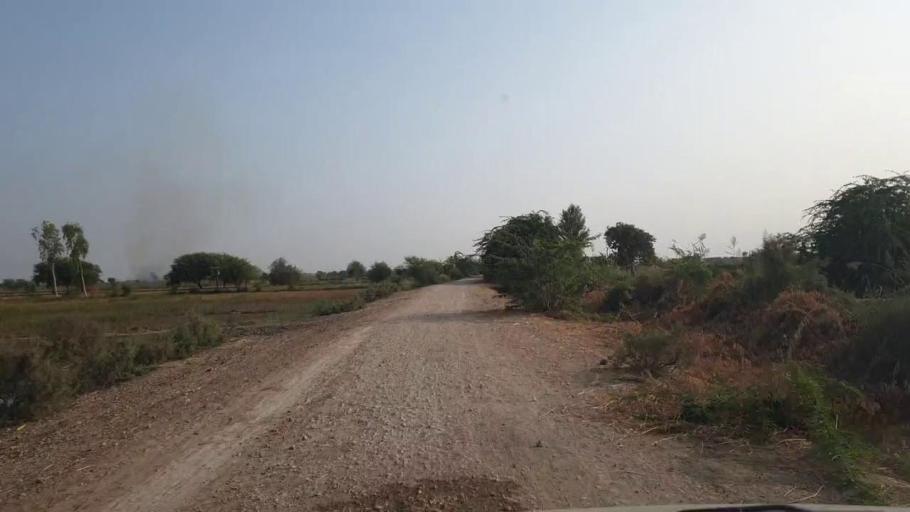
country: PK
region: Sindh
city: Rajo Khanani
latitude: 25.0296
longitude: 68.7782
